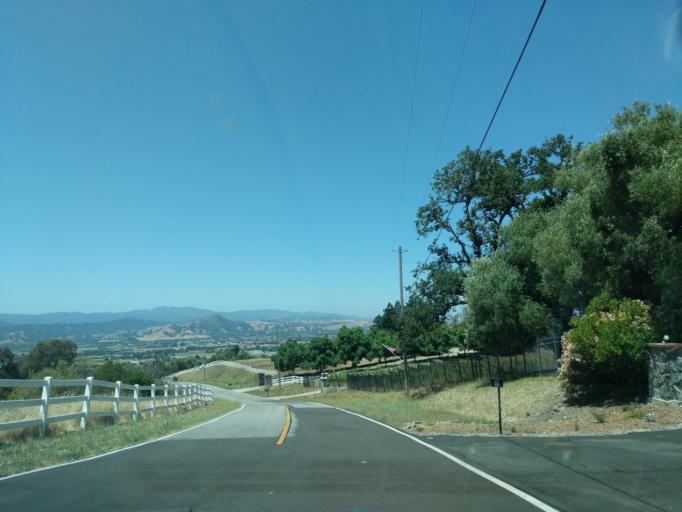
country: US
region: California
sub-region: Santa Clara County
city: San Martin
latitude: 37.1157
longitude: -121.5764
